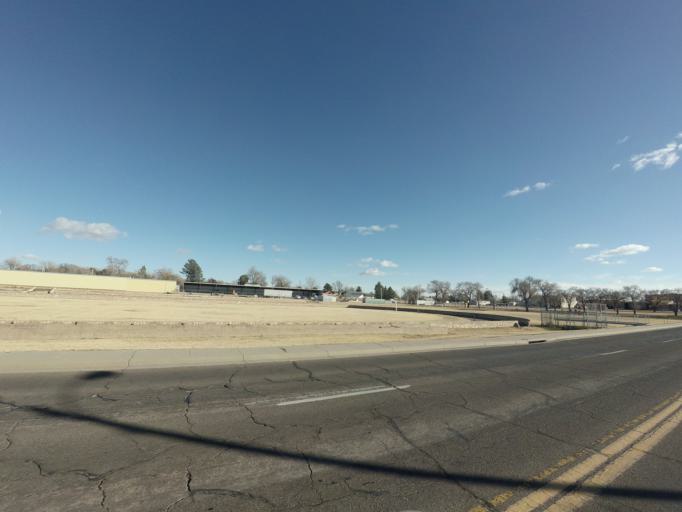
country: US
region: New Mexico
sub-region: Curry County
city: Clovis
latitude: 34.4179
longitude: -103.2054
